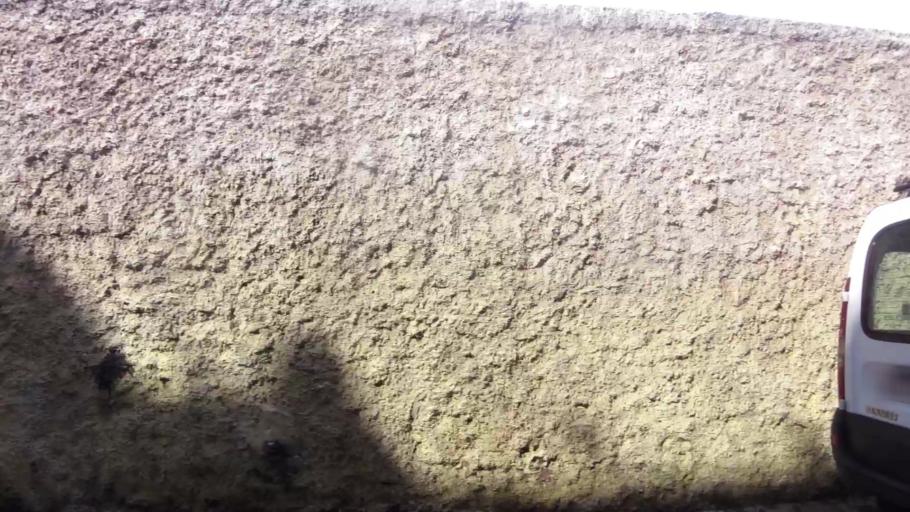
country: MA
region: Grand Casablanca
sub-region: Nouaceur
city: Bouskoura
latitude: 33.5285
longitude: -7.6777
